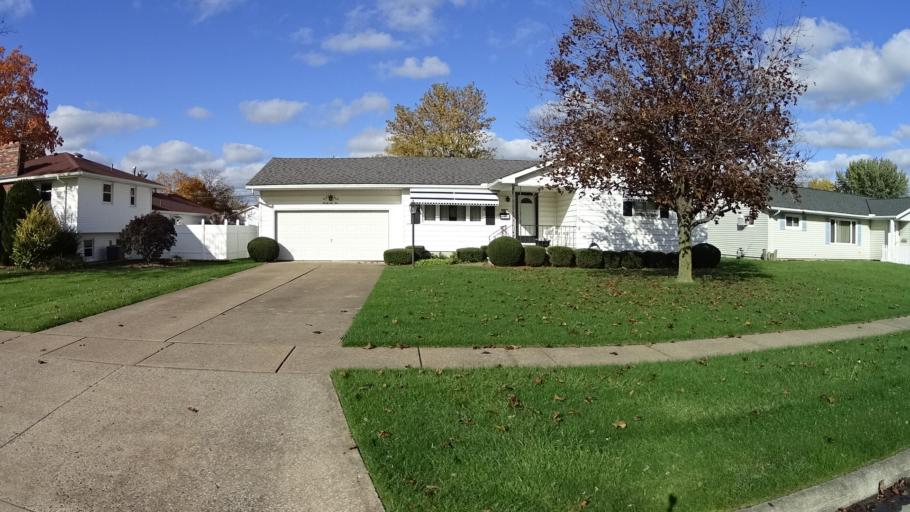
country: US
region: Ohio
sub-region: Lorain County
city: Lorain
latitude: 41.4361
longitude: -82.2005
